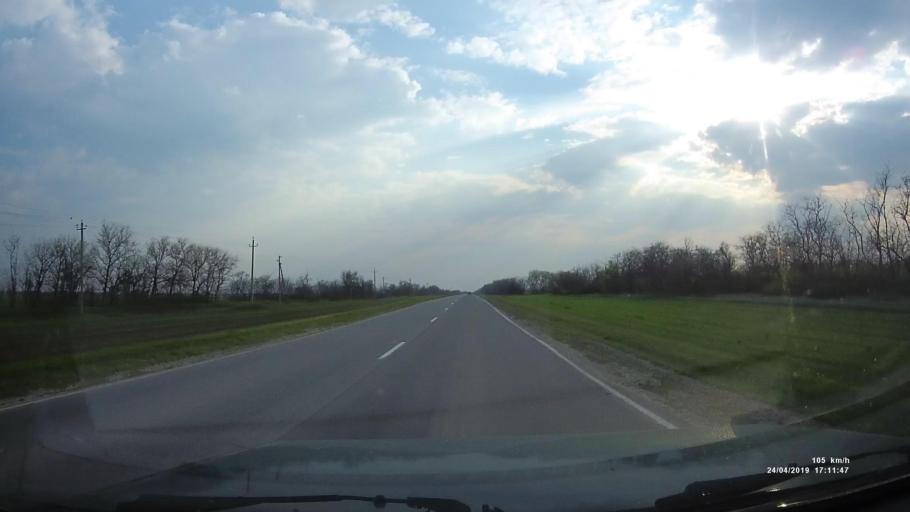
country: RU
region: Rostov
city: Sal'sk
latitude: 46.4898
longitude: 41.5032
